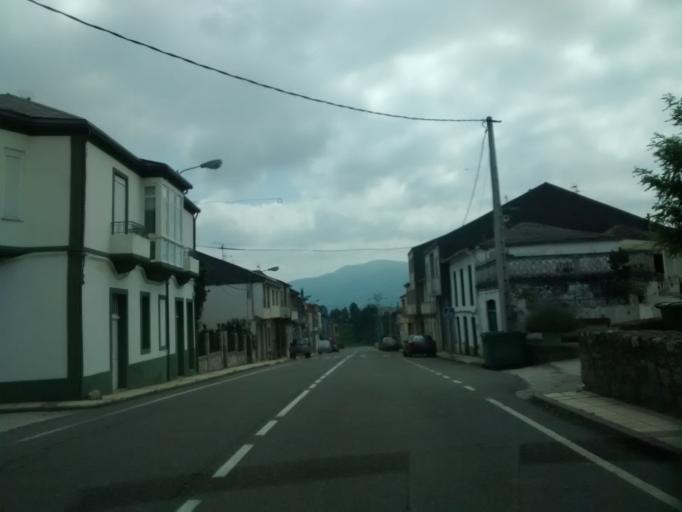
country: ES
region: Galicia
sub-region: Provincia de Ourense
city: Petin
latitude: 42.3466
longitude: -7.1622
